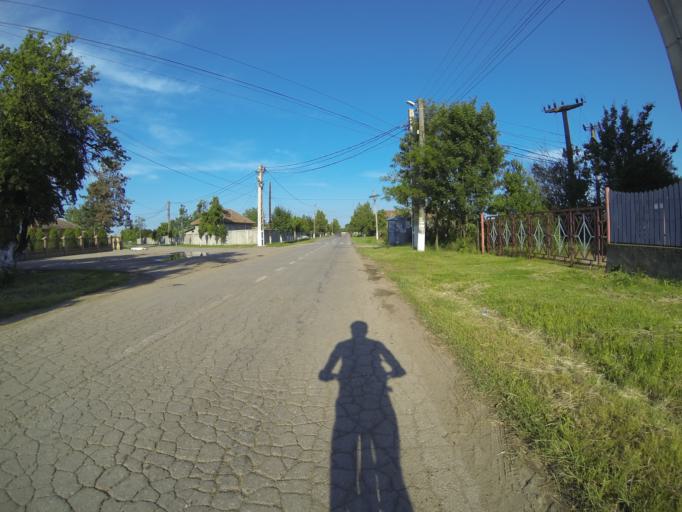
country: RO
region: Dolj
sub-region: Comuna Caloparu
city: Calopar
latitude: 44.1644
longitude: 23.7571
